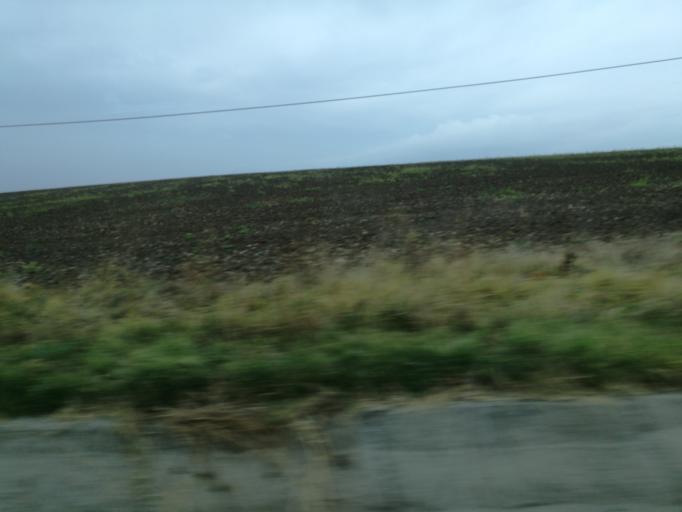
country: RO
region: Tulcea
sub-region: Comuna Horia
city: Horia
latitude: 44.9753
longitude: 28.4419
